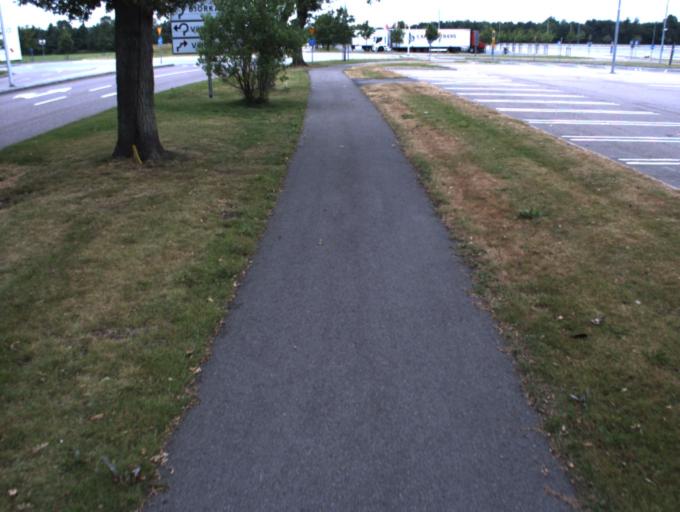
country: SE
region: Skane
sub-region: Helsingborg
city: Odakra
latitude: 56.0907
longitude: 12.7529
